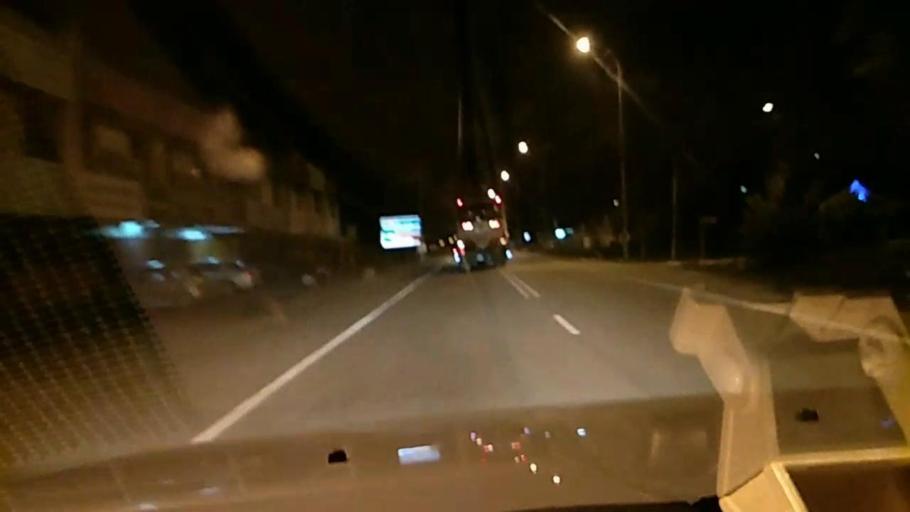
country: MY
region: Selangor
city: Kuala Selangor
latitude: 3.3090
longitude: 101.3147
